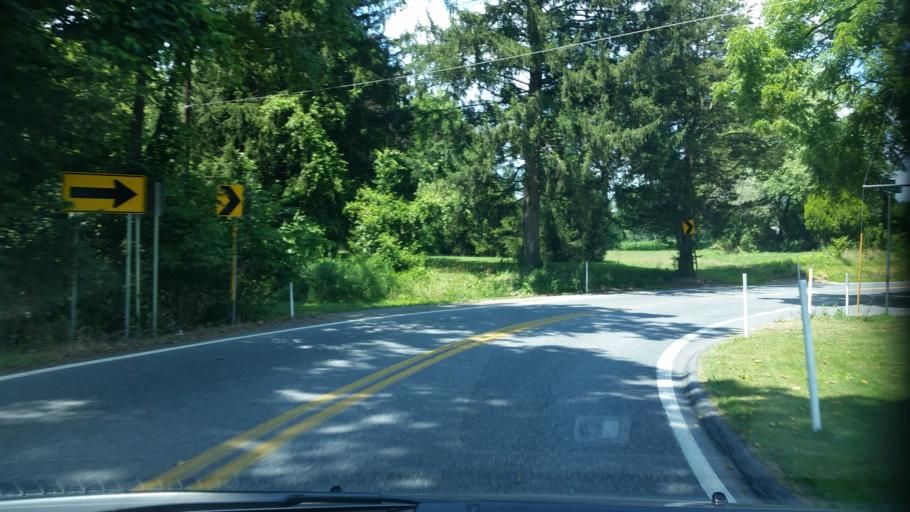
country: US
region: Pennsylvania
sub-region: Dauphin County
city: Hummelstown
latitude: 40.2885
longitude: -76.6875
